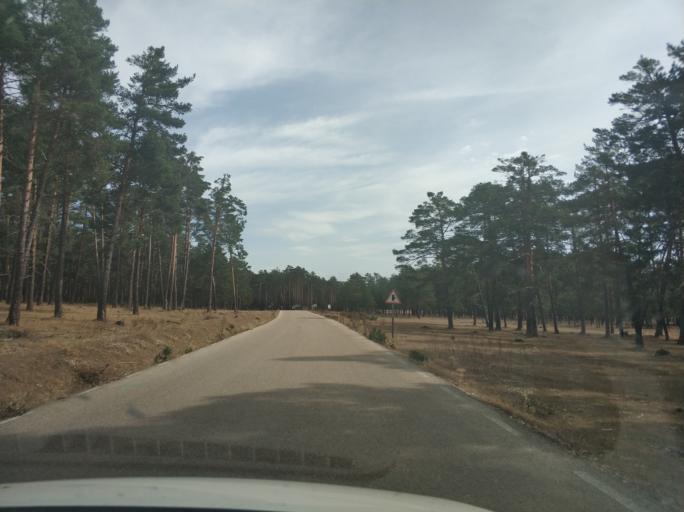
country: ES
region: Castille and Leon
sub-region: Provincia de Soria
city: Navaleno
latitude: 41.8592
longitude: -2.9418
